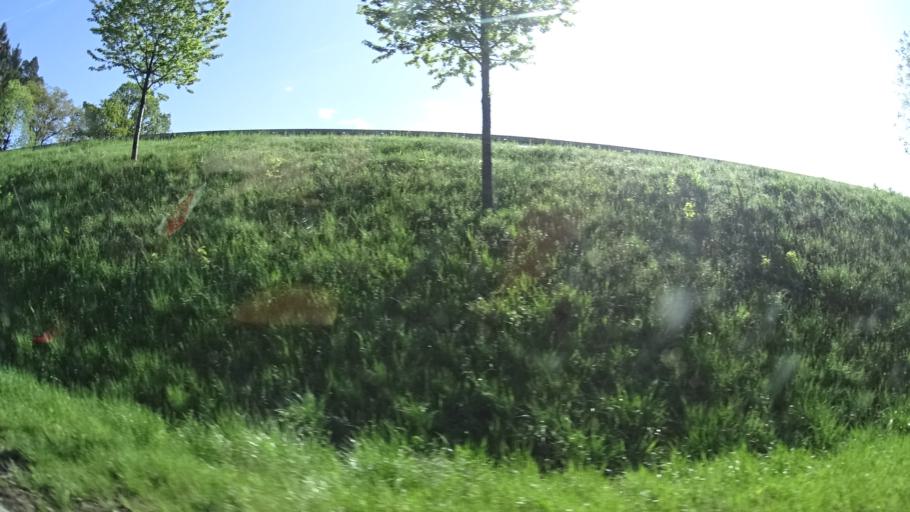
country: DE
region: Baden-Wuerttemberg
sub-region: Regierungsbezirk Stuttgart
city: Motzingen
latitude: 48.5166
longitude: 8.7767
